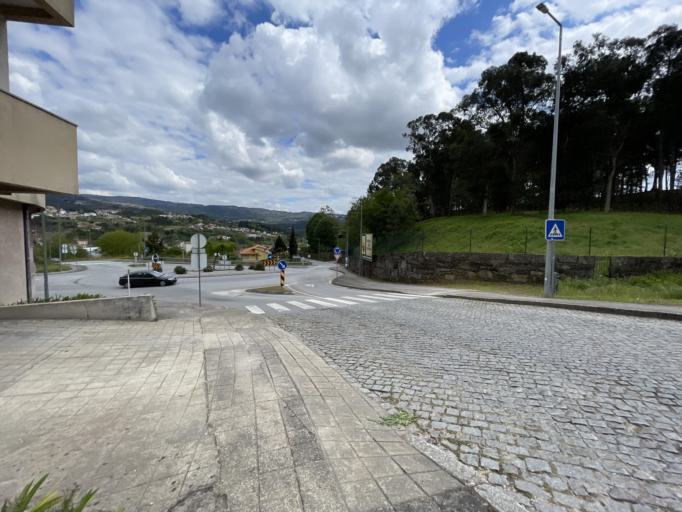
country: PT
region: Porto
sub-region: Marco de Canaveses
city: Marco de Canavezes
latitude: 41.1822
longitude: -8.1429
